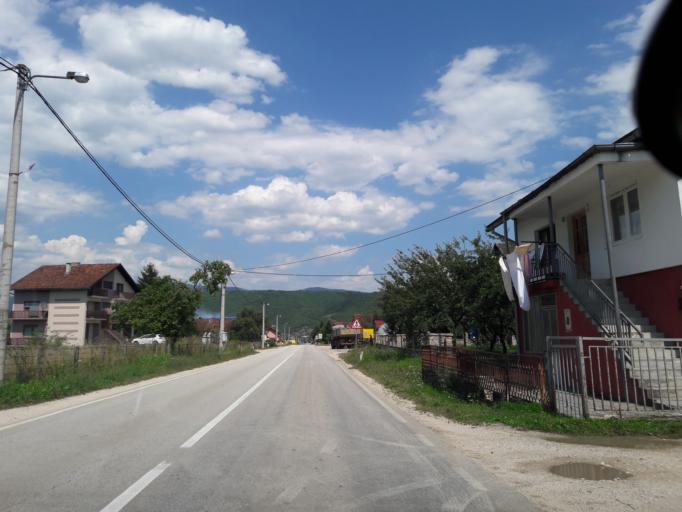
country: BA
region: Republika Srpska
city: Mrkonjic Grad
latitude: 44.4343
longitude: 17.1461
